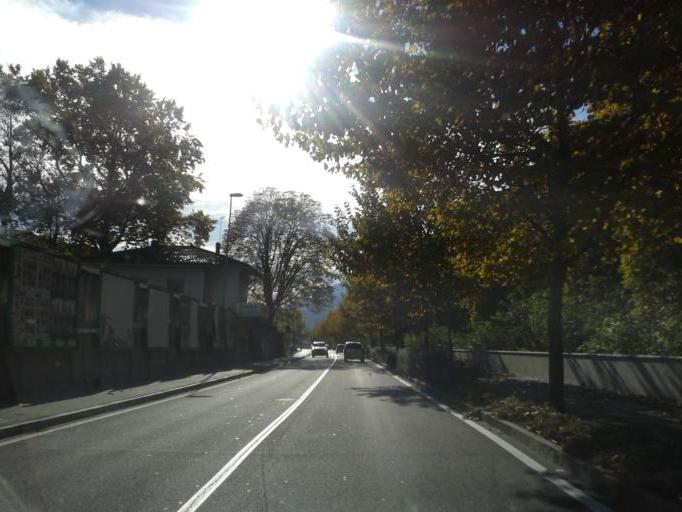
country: IT
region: Trentino-Alto Adige
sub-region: Provincia di Trento
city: Trento
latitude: 46.0642
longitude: 11.1134
